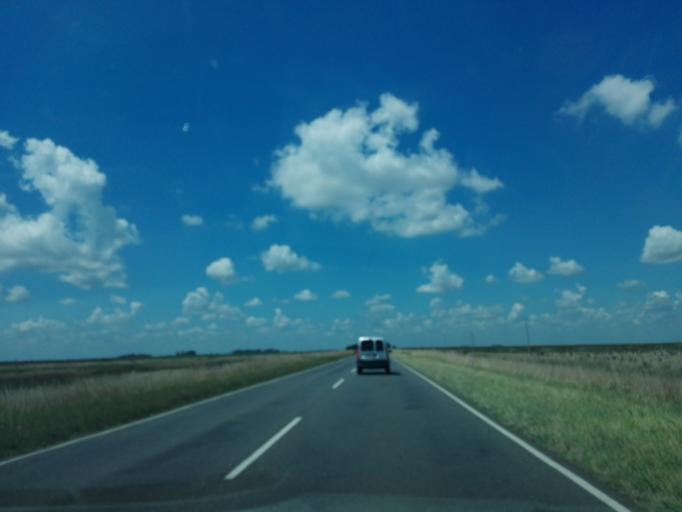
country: AR
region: Buenos Aires
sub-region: Partido de General Belgrano
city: General Belgrano
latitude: -35.9041
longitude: -58.6190
